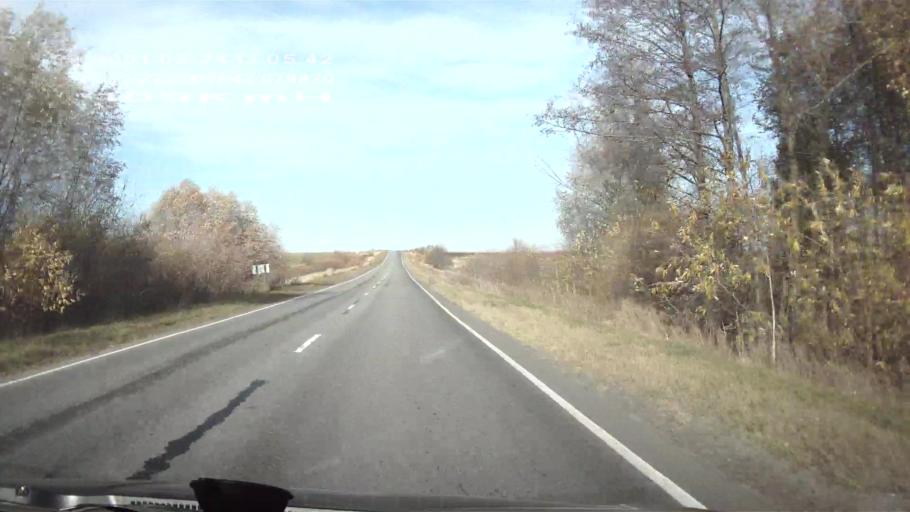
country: RU
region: Chuvashia
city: Ibresi
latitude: 55.2736
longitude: 47.0798
